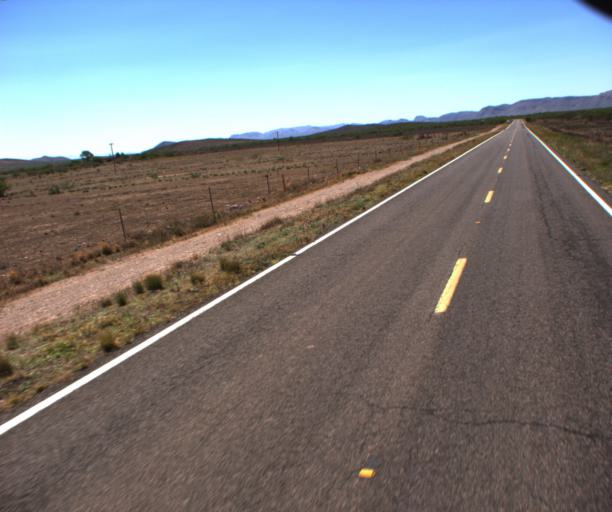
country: US
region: Arizona
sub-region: Cochise County
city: Douglas
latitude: 31.5211
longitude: -109.3038
